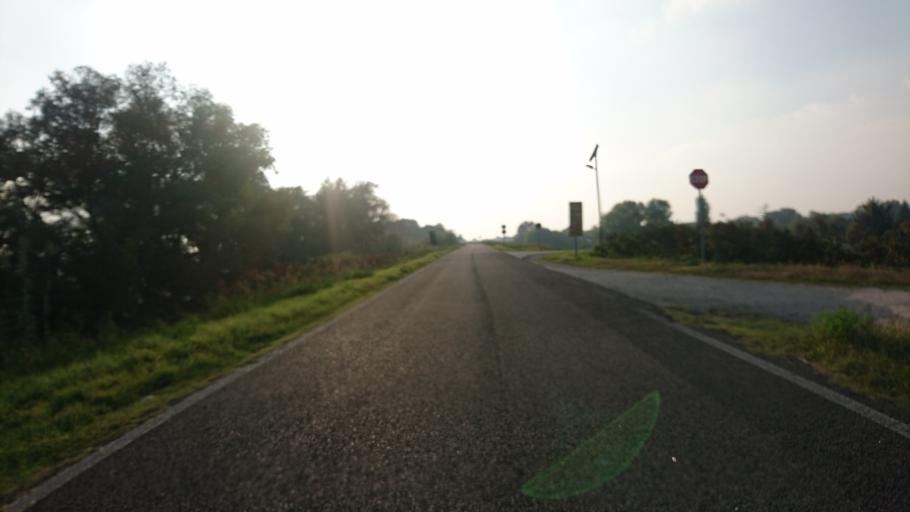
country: IT
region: Veneto
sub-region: Provincia di Rovigo
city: Canaro
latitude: 44.9194
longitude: 11.6839
